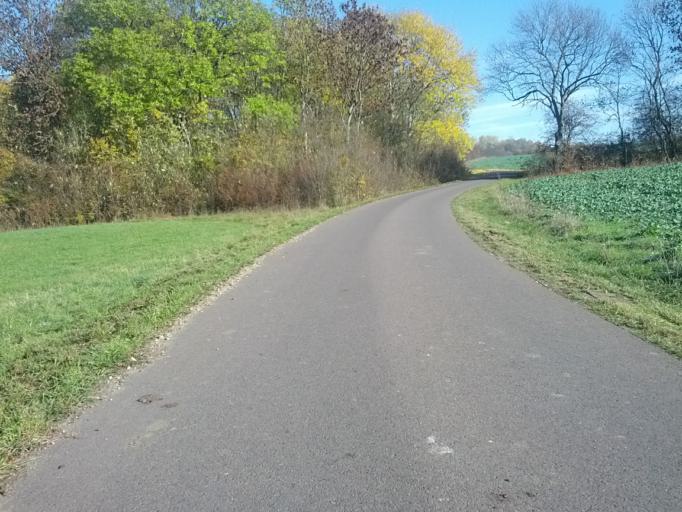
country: DE
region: Thuringia
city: Seebach
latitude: 50.9967
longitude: 10.4341
